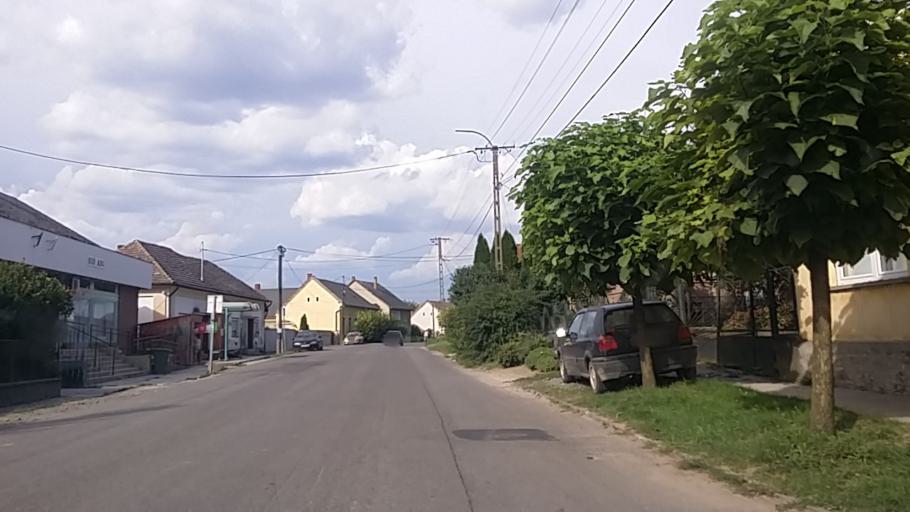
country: HU
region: Tolna
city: Zomba
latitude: 46.5090
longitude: 18.5881
